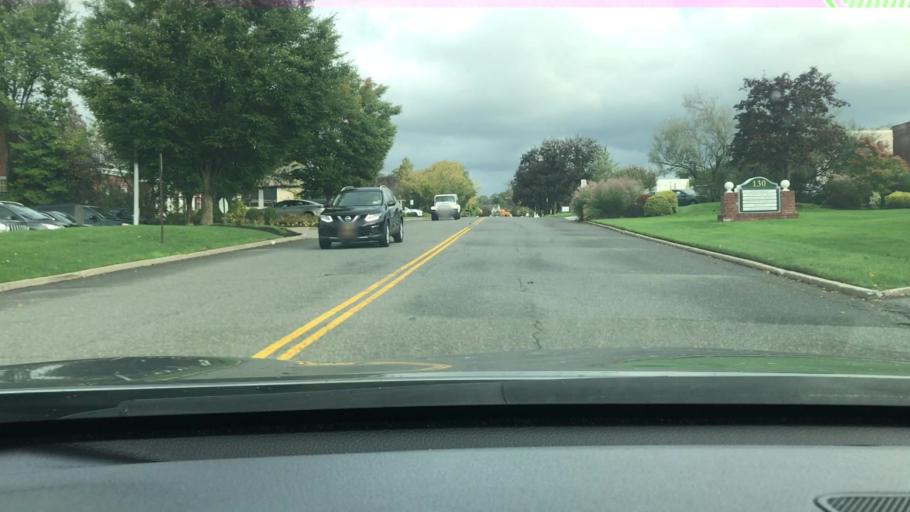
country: US
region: New York
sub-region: Nassau County
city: Syosset
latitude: 40.8088
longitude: -73.4856
